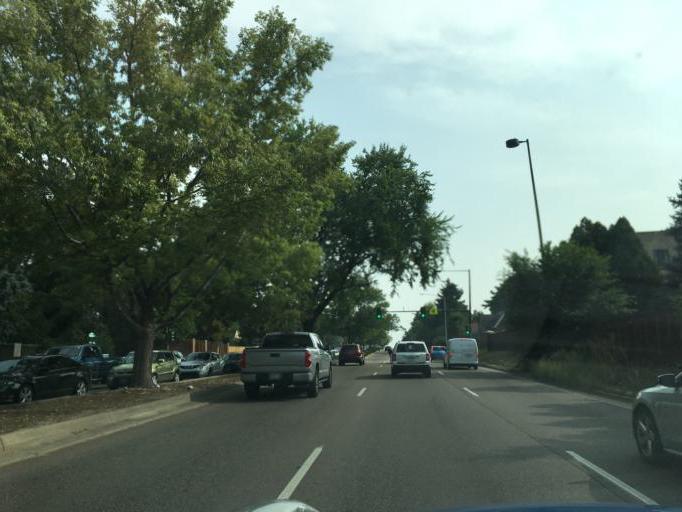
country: US
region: Colorado
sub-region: Arapahoe County
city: Glendale
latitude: 39.7250
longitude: -104.9408
